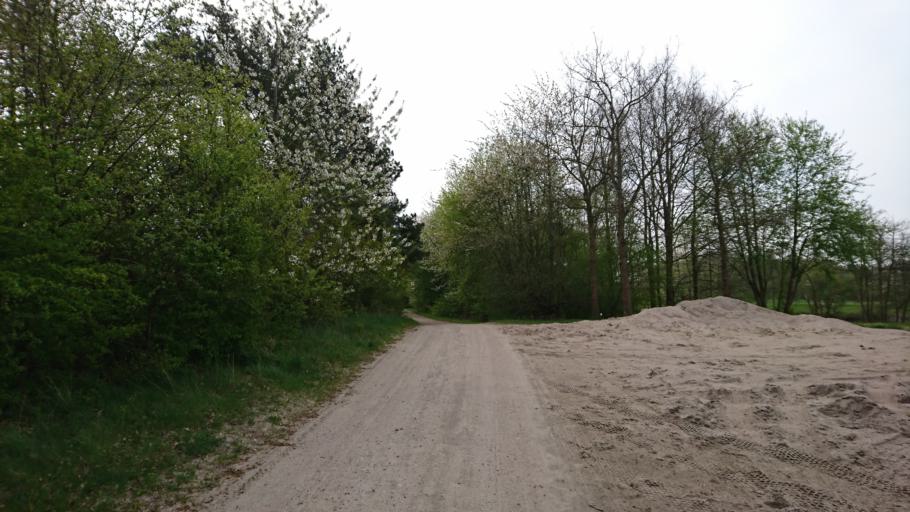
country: DK
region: Capital Region
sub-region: Ballerup Kommune
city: Ballerup
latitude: 55.7462
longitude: 12.3972
